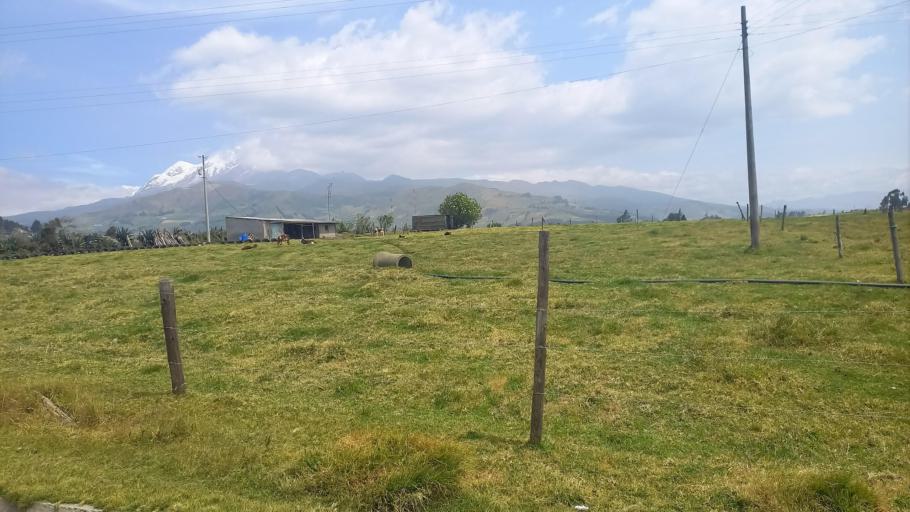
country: EC
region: Pichincha
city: Cayambe
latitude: 0.1577
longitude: -78.0735
